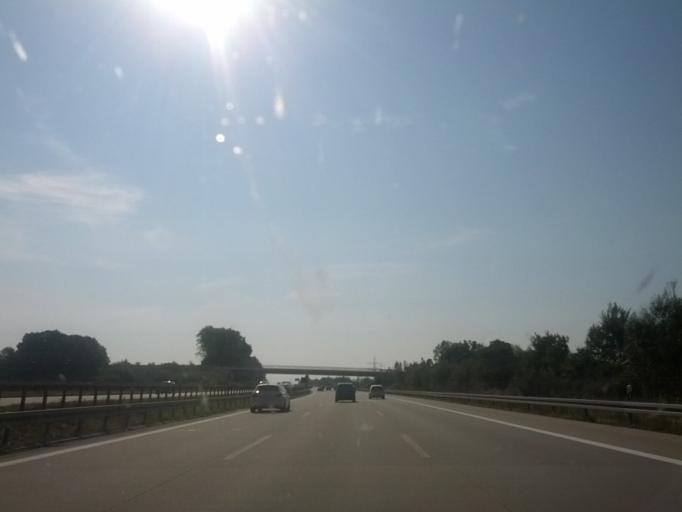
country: DE
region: Brandenburg
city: Hoppegarten
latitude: 52.5648
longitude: 13.6524
